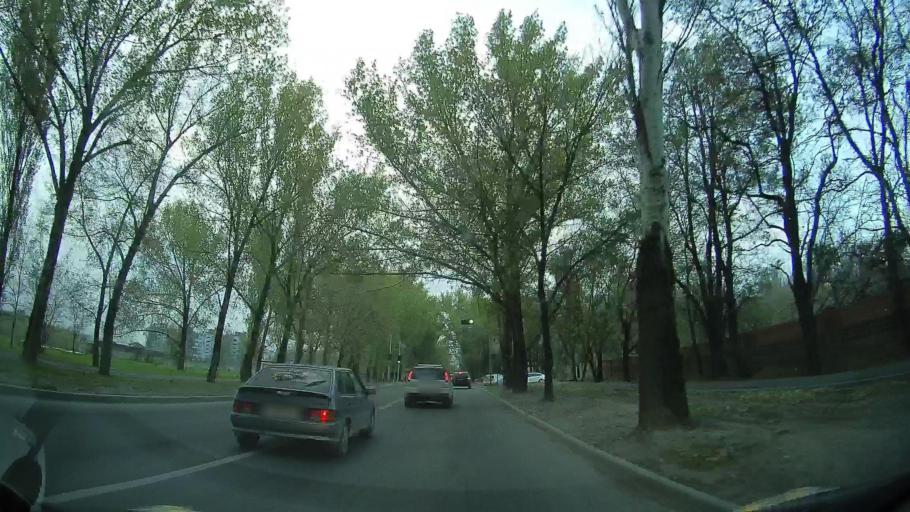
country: RU
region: Rostov
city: Severnyy
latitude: 47.2714
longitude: 39.6647
